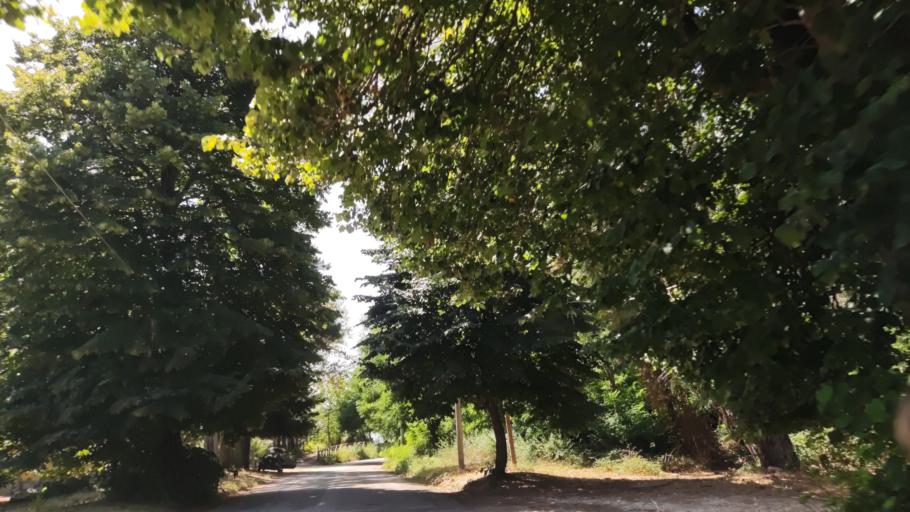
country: IT
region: Calabria
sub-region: Provincia di Reggio Calabria
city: Seminara
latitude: 38.3391
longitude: 15.8453
